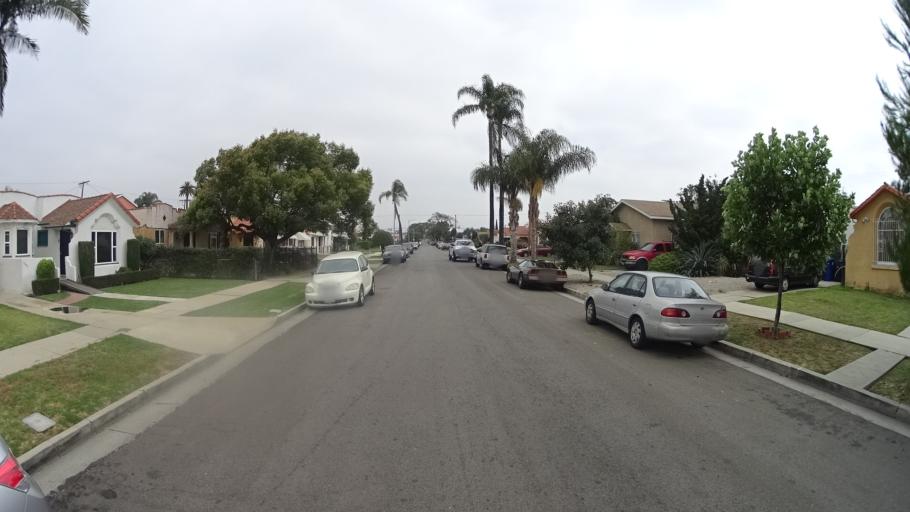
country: US
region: California
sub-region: Los Angeles County
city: View Park-Windsor Hills
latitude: 34.0262
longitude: -118.3374
